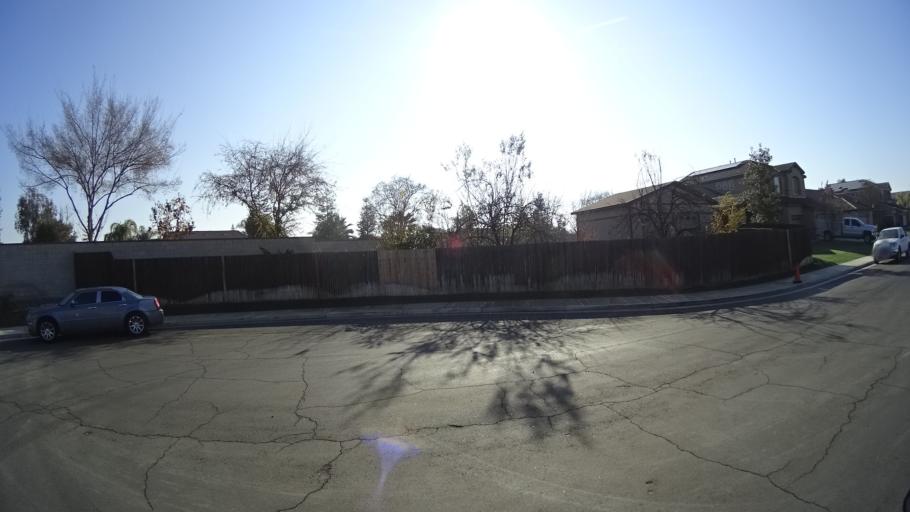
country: US
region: California
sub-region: Kern County
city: Greenacres
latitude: 35.3095
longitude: -119.1192
